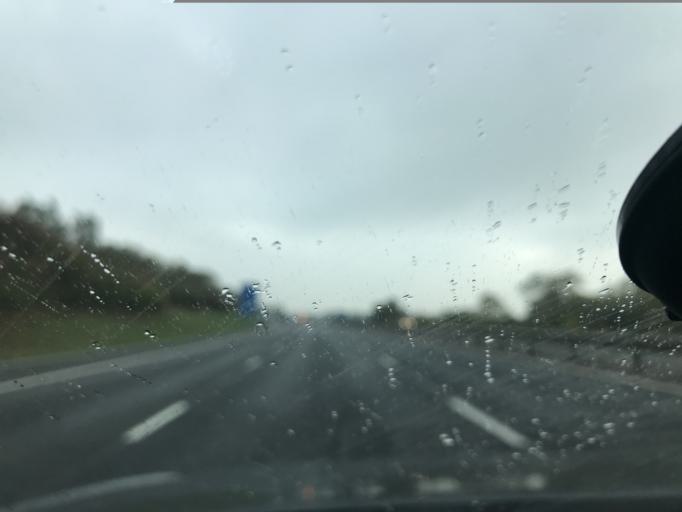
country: GB
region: England
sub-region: Oxfordshire
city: Wheatley
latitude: 51.7527
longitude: -1.1053
